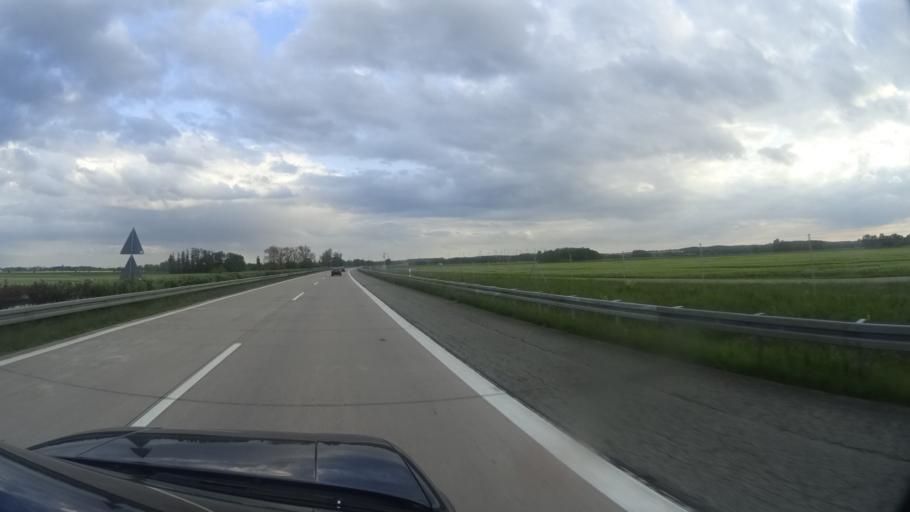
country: DE
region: Brandenburg
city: Wittstock
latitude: 53.1878
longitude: 12.4570
